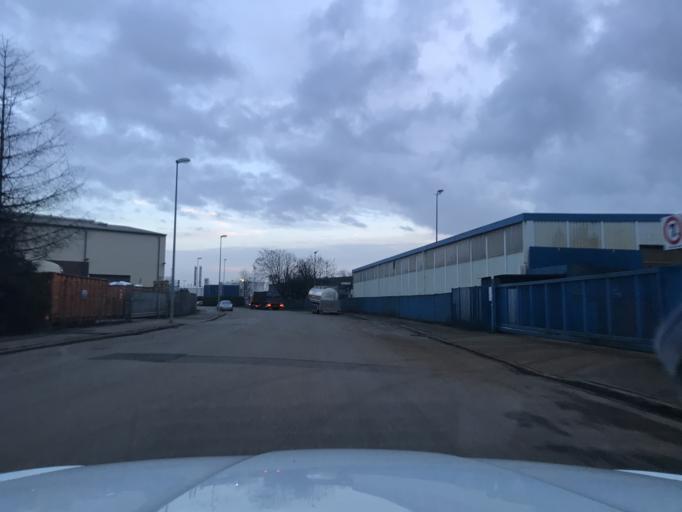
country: DE
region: North Rhine-Westphalia
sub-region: Regierungsbezirk Dusseldorf
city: Muelheim (Ruhr)
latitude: 51.4390
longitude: 6.8401
